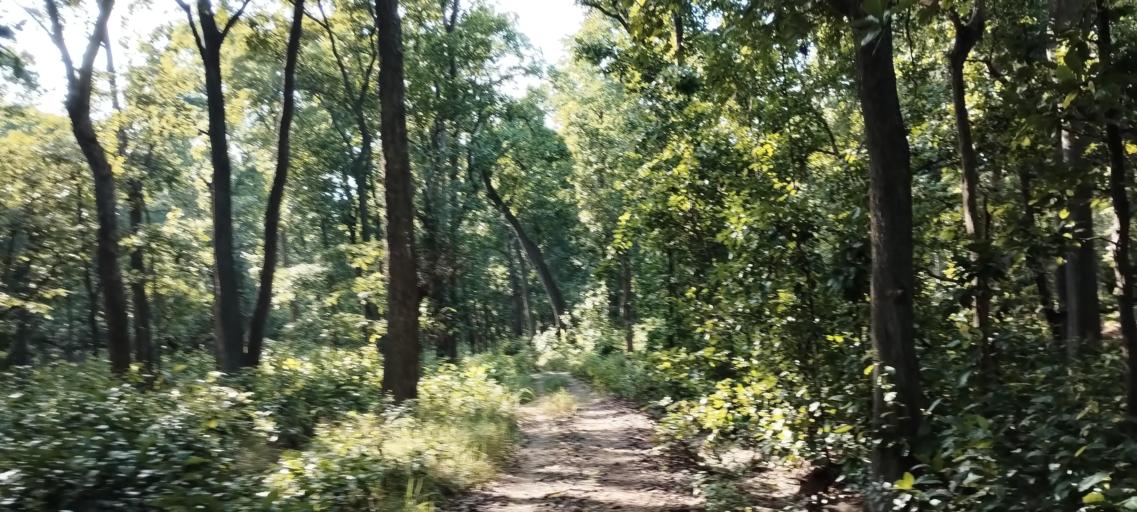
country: NP
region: Far Western
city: Tikapur
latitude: 28.5229
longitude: 81.2629
